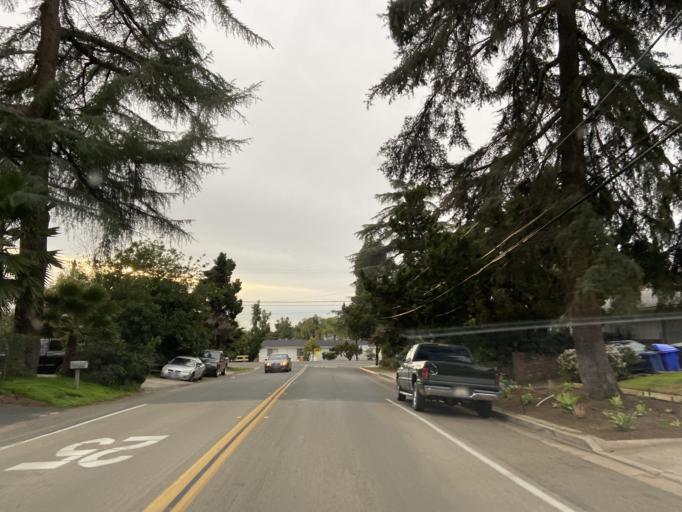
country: US
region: California
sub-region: San Diego County
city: Escondido
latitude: 33.1044
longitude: -117.0658
